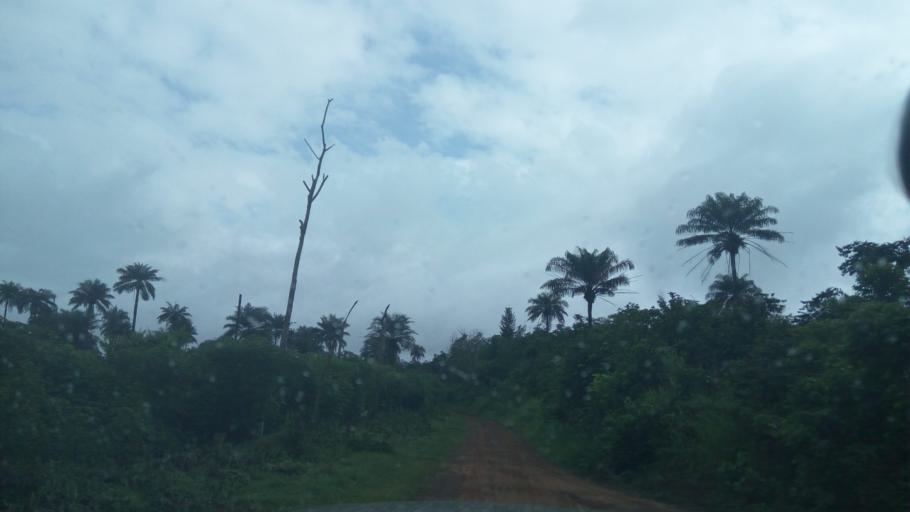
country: SL
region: Southern Province
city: Bomi
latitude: 7.3101
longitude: -11.6020
